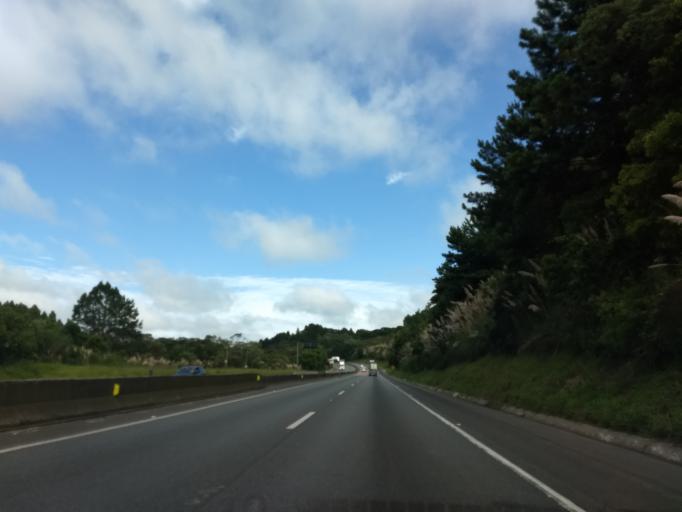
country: BR
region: Parana
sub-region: Sao Jose Dos Pinhais
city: Sao Jose dos Pinhais
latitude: -25.8463
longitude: -49.0852
